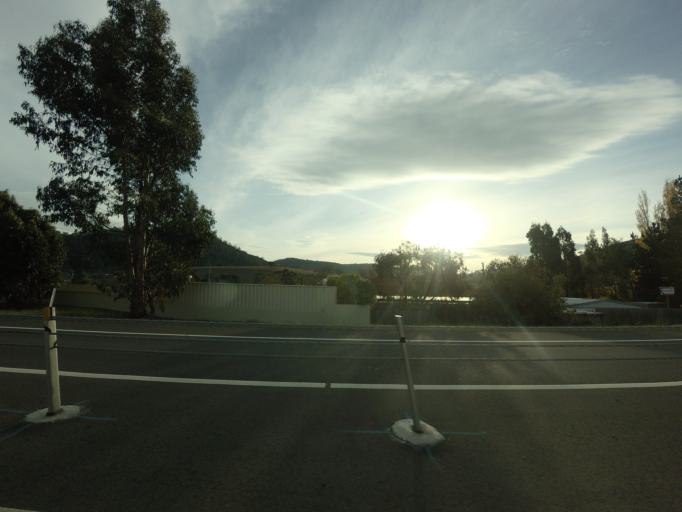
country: AU
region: Tasmania
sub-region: Brighton
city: Bridgewater
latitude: -42.5944
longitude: 147.2218
